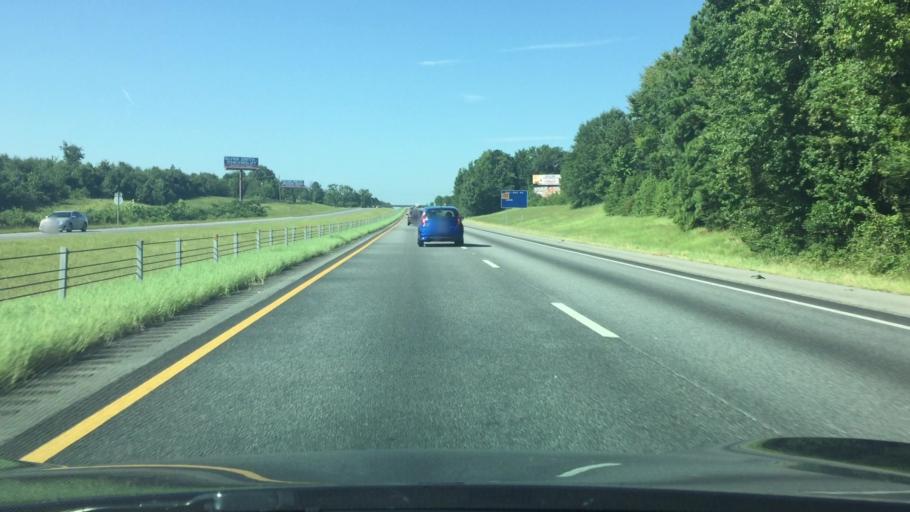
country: US
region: Alabama
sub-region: Lee County
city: Opelika
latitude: 32.6800
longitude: -85.3261
